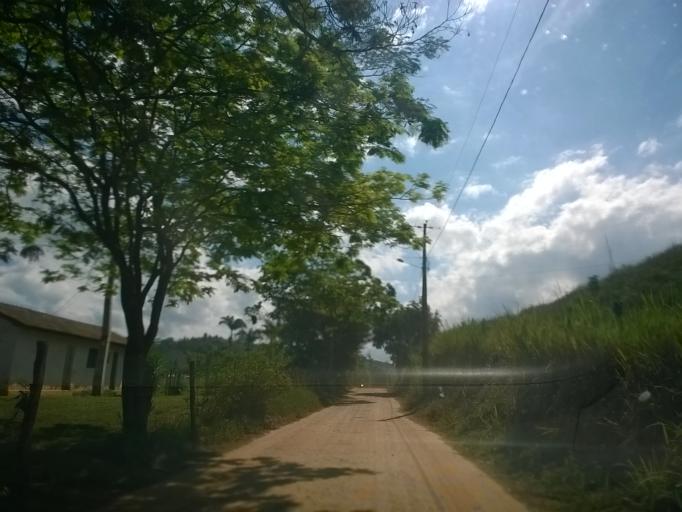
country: BR
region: Minas Gerais
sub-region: Uba
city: Uba
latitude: -21.0680
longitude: -42.9012
